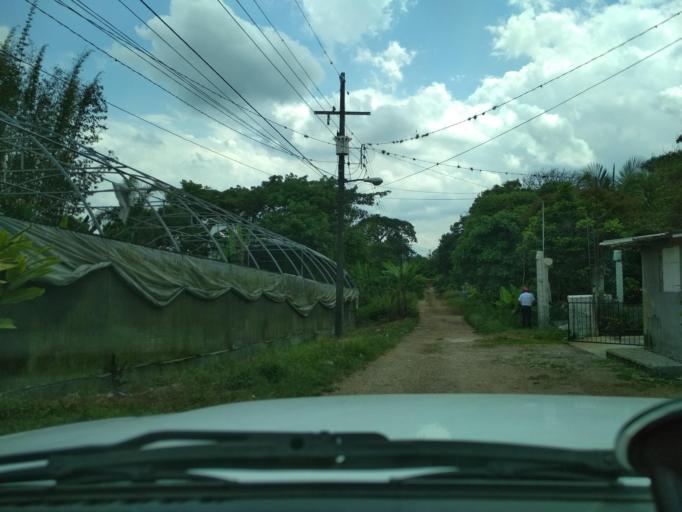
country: MX
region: Veracruz
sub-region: Cordoba
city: San Jose de Abajo [Unidad Habitacional]
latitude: 18.9159
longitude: -96.9596
